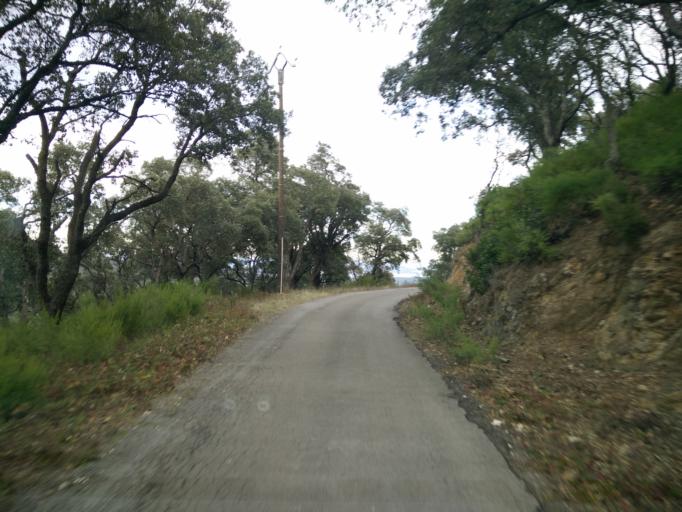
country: FR
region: Provence-Alpes-Cote d'Azur
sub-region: Departement du Var
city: Roquebrune-sur-Argens
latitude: 43.3825
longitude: 6.6140
